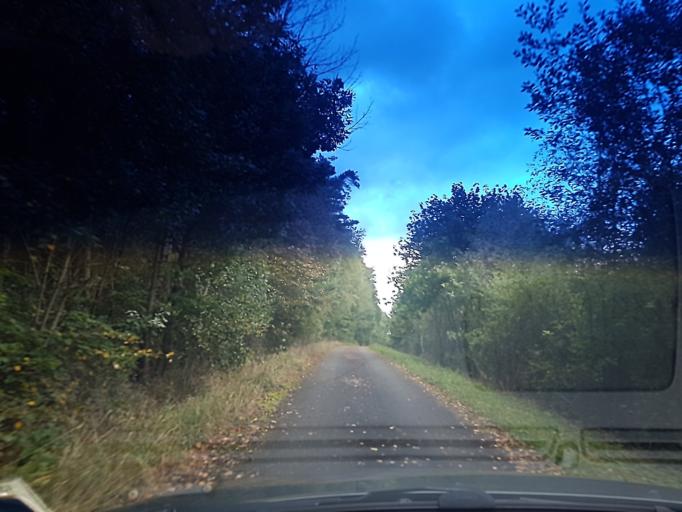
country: DE
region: Bavaria
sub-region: Upper Franconia
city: Strullendorf
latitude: 49.8509
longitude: 10.9867
